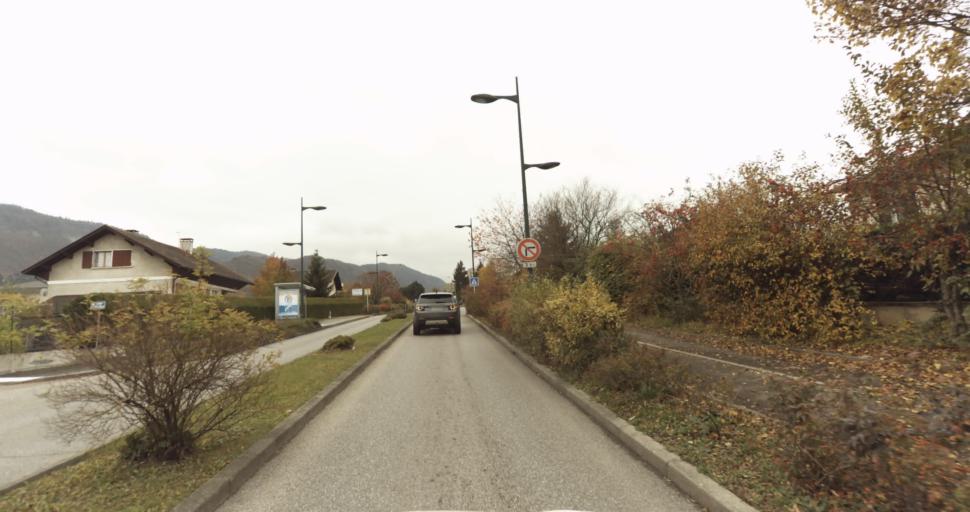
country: FR
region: Rhone-Alpes
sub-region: Departement de la Haute-Savoie
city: Annecy
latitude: 45.8834
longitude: 6.1085
